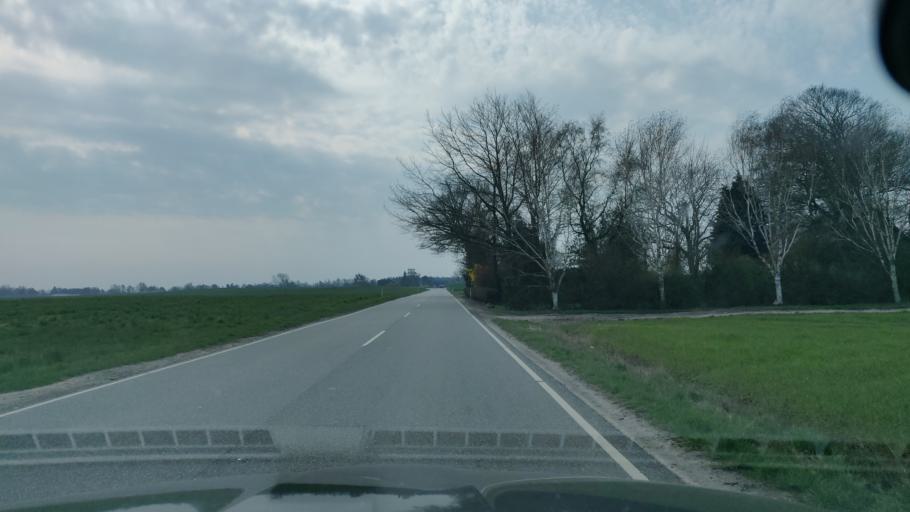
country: DK
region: South Denmark
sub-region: Nordfyns Kommune
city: Sonderso
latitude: 55.5001
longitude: 10.2492
